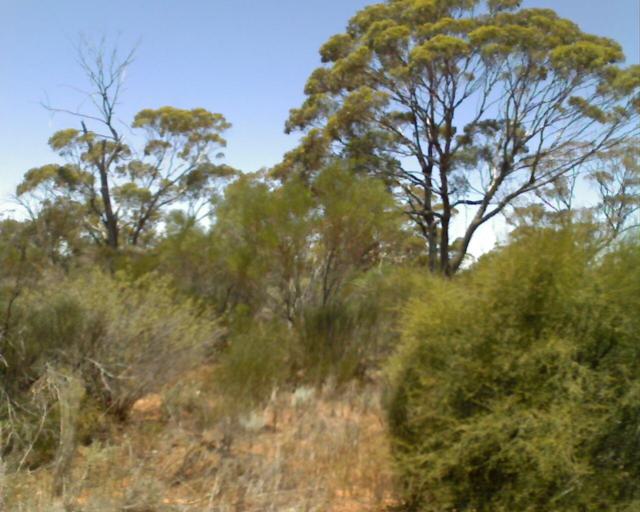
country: AU
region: Western Australia
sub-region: Merredin
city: Merredin
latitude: -30.9618
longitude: 118.8901
